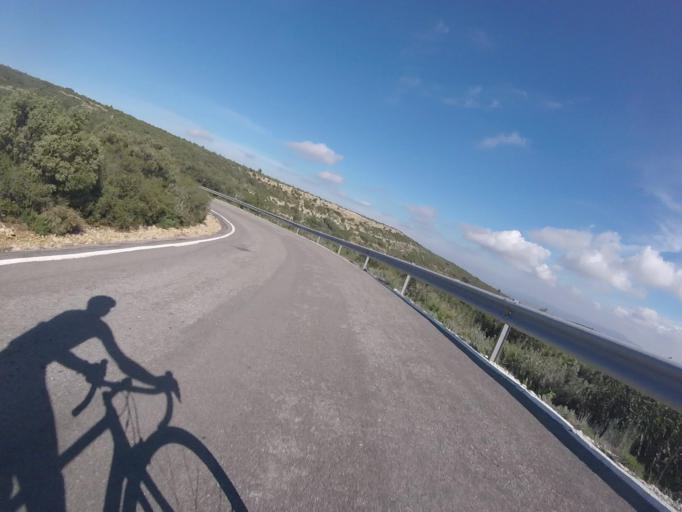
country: ES
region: Valencia
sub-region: Provincia de Castello
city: Albocasser
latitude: 40.3344
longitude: 0.0427
